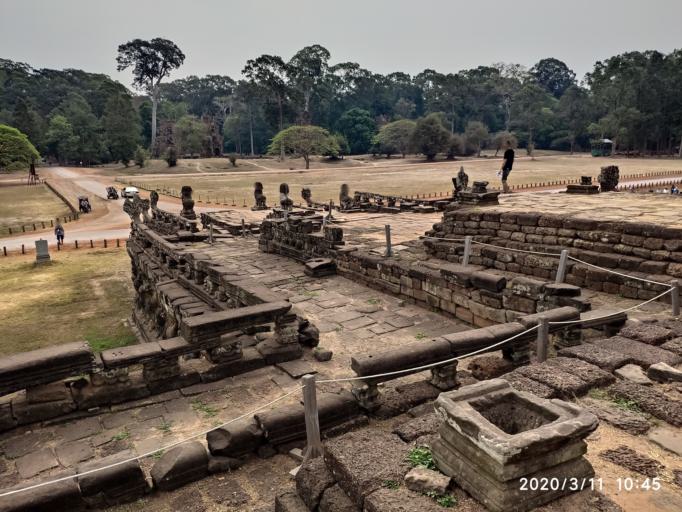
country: KH
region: Siem Reap
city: Siem Reap
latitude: 13.4460
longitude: 103.8588
